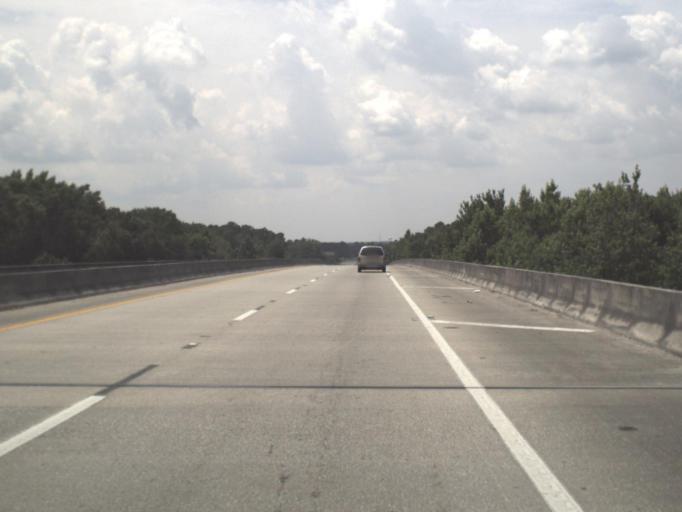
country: US
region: Florida
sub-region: Putnam County
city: Palatka
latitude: 29.6988
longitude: -81.6638
